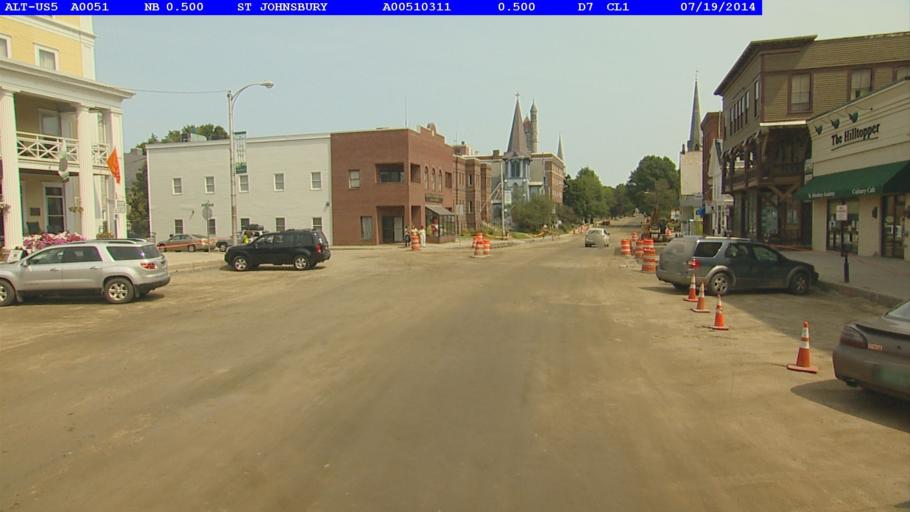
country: US
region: Vermont
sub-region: Caledonia County
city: Saint Johnsbury
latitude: 44.4188
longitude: -72.0210
